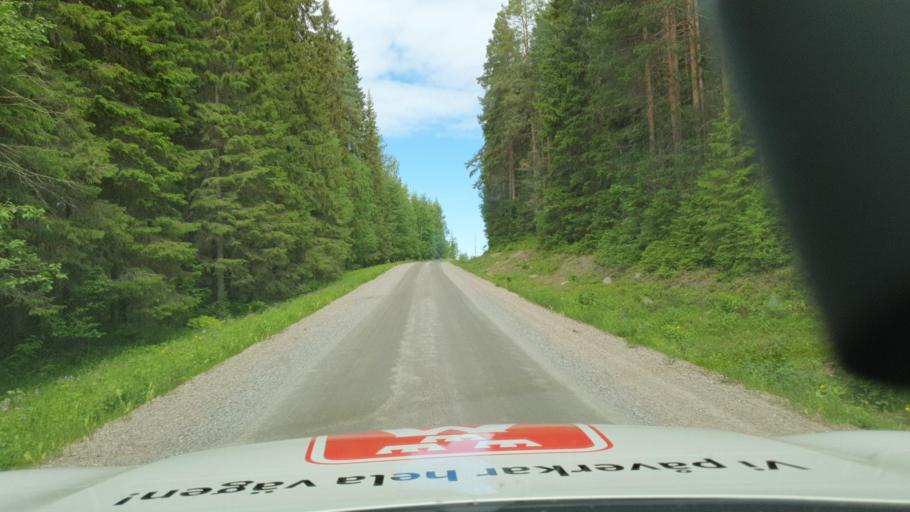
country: SE
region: Vaesterbotten
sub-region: Skelleftea Kommun
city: Forsbacka
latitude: 64.6433
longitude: 20.5404
